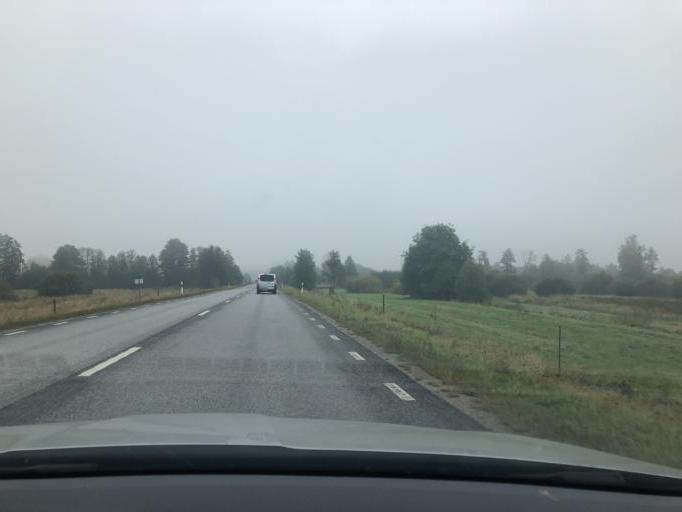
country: SE
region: Uppsala
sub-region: Tierps Kommun
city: Tierp
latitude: 60.3286
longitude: 17.5140
